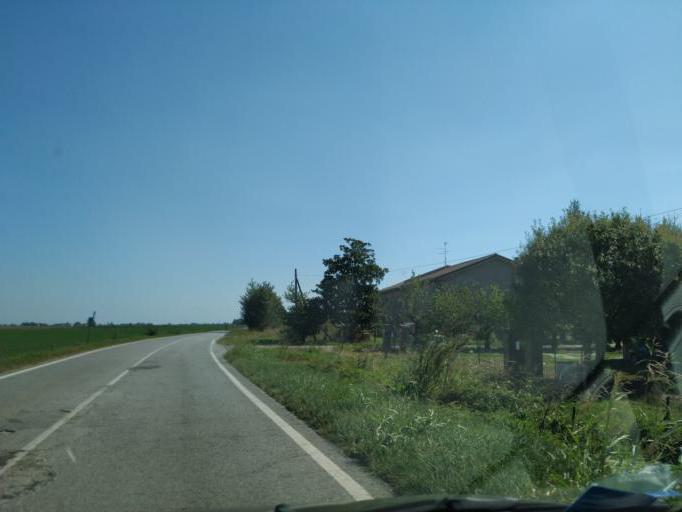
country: IT
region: Emilia-Romagna
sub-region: Provincia di Ferrara
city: Coccanile-Cesta
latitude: 44.8875
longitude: 11.8957
